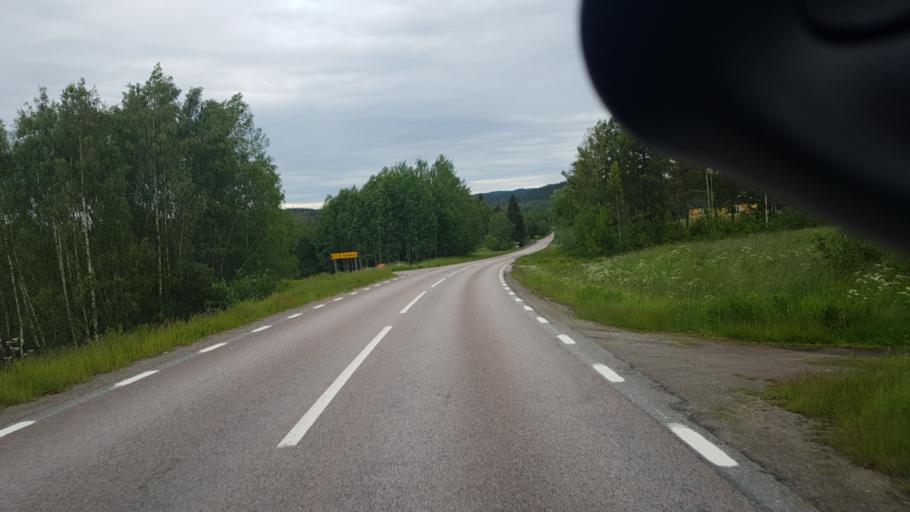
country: SE
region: Vaermland
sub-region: Eda Kommun
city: Amotfors
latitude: 59.7246
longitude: 12.2803
